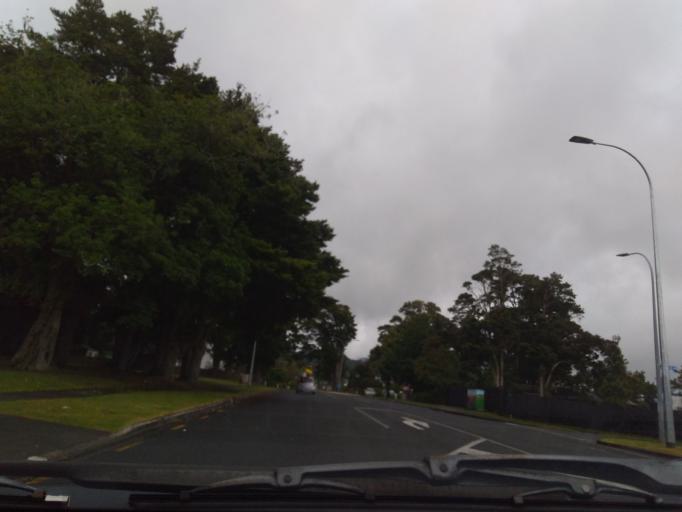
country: NZ
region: Northland
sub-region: Whangarei
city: Whangarei
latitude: -35.6820
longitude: 174.3205
